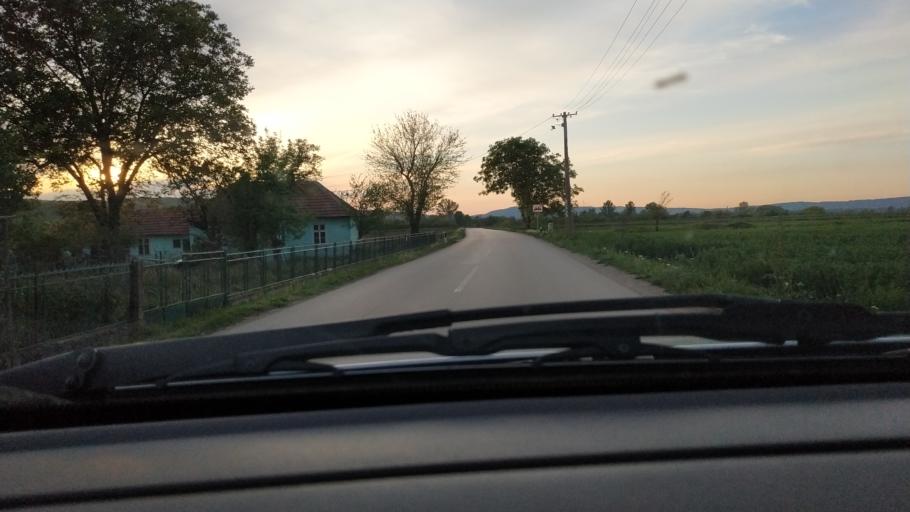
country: RS
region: Central Serbia
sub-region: Nisavski Okrug
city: Aleksinac
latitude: 43.5459
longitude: 21.6241
